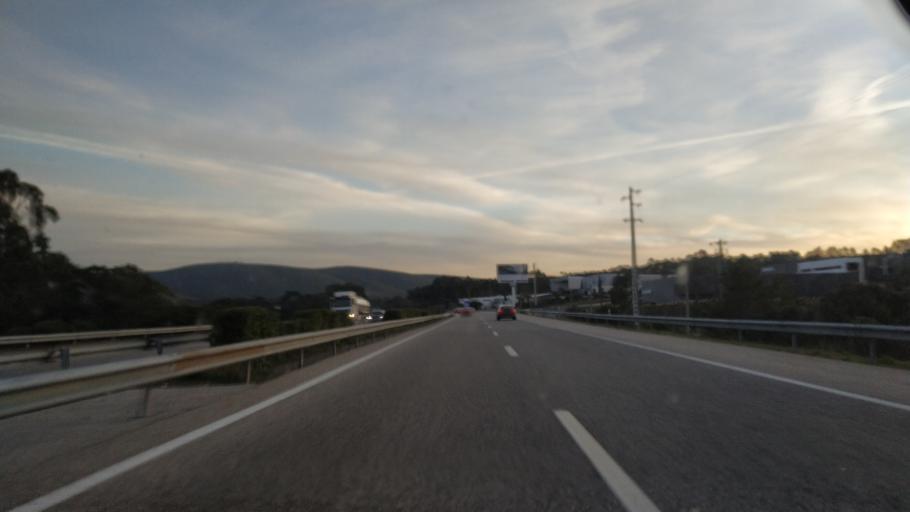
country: PT
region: Santarem
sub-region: Ourem
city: Fatima
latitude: 39.5702
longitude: -8.6525
